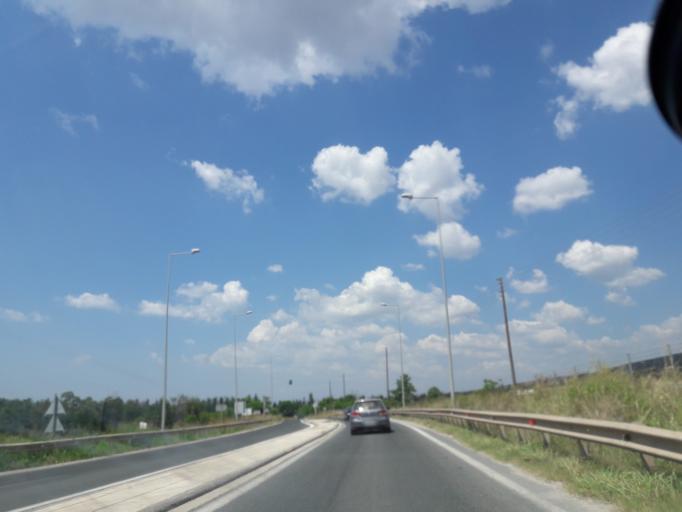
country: GR
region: Central Macedonia
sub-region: Nomos Thessalonikis
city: Souroti
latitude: 40.5067
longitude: 23.0889
